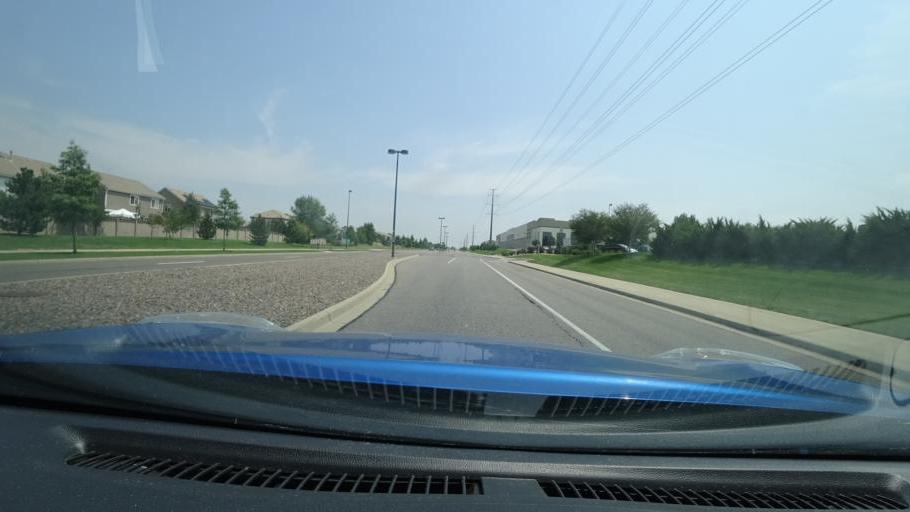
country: US
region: Colorado
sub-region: Adams County
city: Aurora
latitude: 39.7692
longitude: -104.7618
